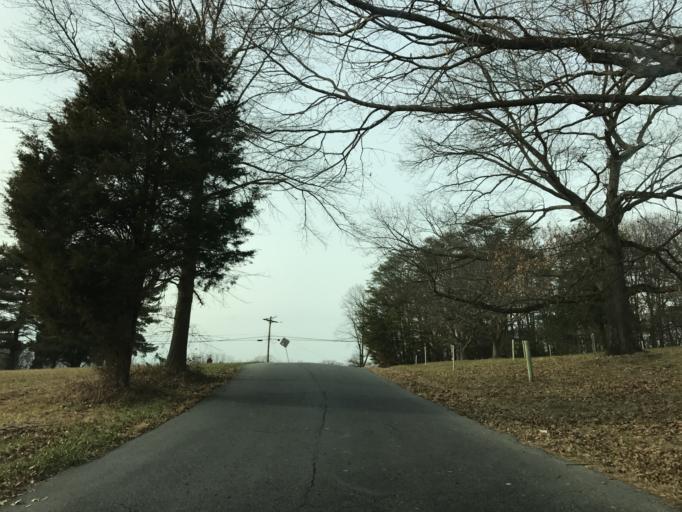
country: US
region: Maryland
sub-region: Baltimore County
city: White Marsh
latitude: 39.3884
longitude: -76.3978
